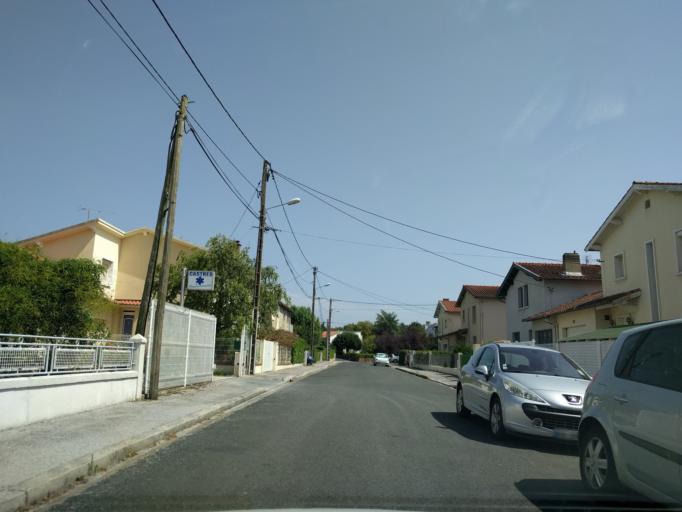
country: FR
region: Midi-Pyrenees
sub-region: Departement du Tarn
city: Castres
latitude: 43.5967
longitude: 2.2446
